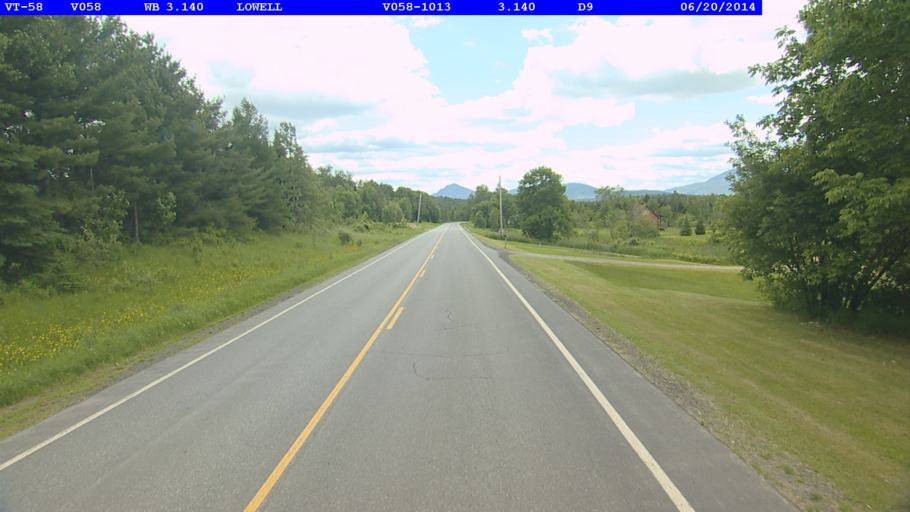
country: US
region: Vermont
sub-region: Orleans County
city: Newport
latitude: 44.8151
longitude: -72.3961
